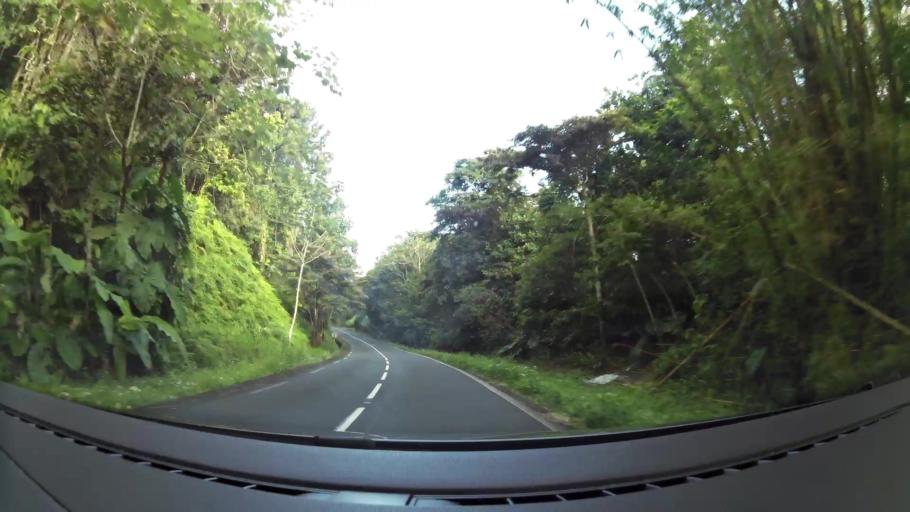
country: GP
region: Guadeloupe
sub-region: Guadeloupe
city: Bouillante
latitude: 16.1793
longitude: -61.7119
